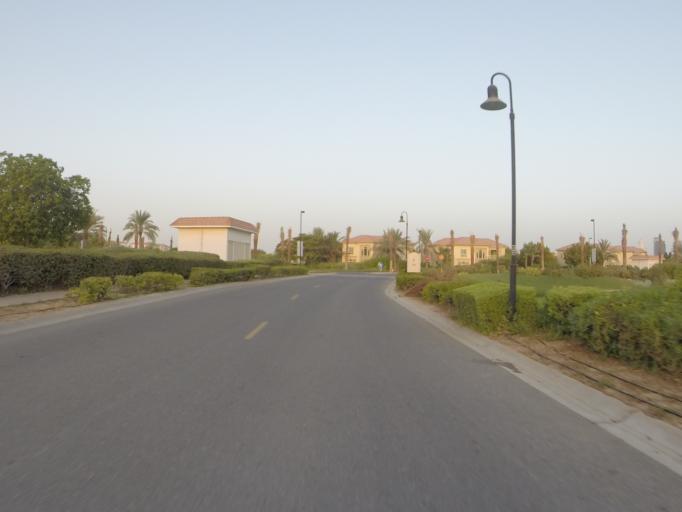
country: AE
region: Dubai
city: Dubai
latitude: 25.0571
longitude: 55.1605
